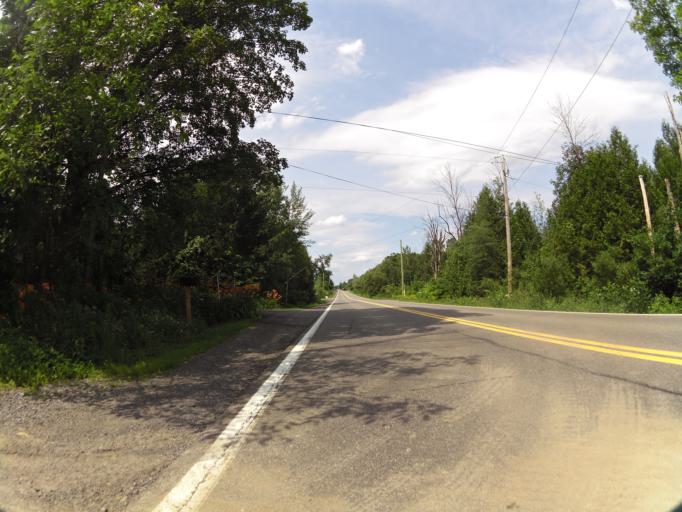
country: CA
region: Ontario
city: Ottawa
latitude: 45.2278
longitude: -75.6072
